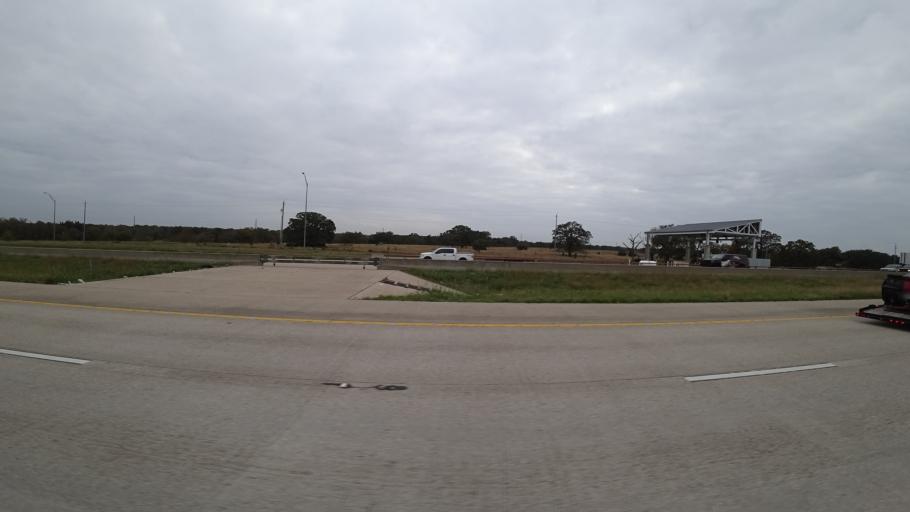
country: US
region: Texas
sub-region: Williamson County
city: Brushy Creek
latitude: 30.4803
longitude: -97.7375
